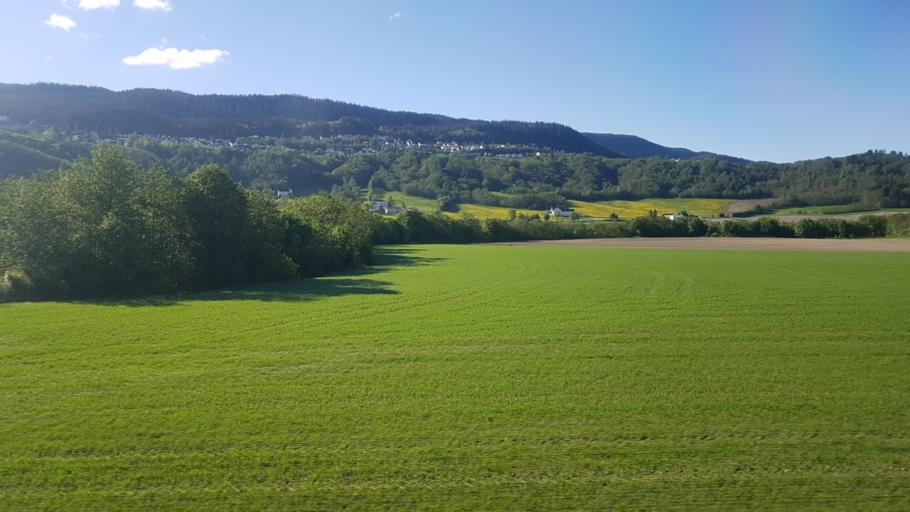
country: NO
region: Sor-Trondelag
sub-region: Melhus
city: Melhus
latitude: 63.3121
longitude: 10.3008
